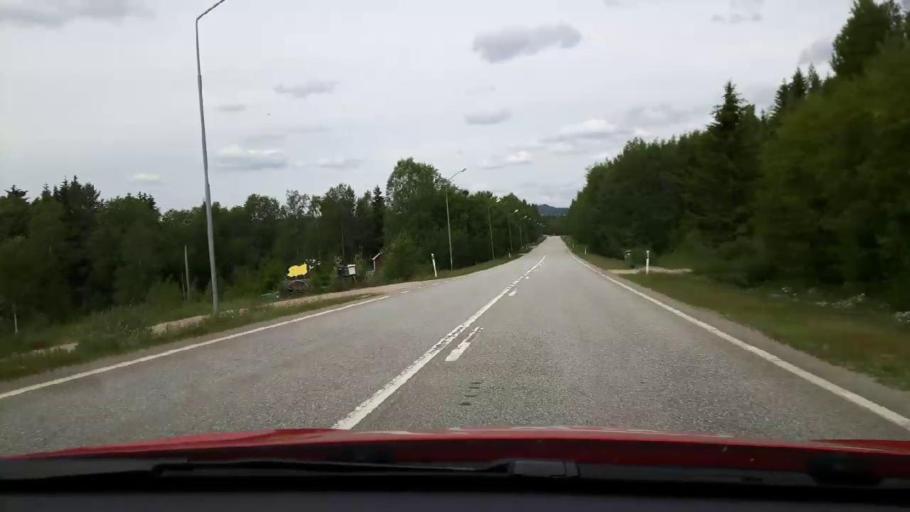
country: SE
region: Jaemtland
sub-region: Harjedalens Kommun
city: Sveg
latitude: 62.0675
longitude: 14.2728
